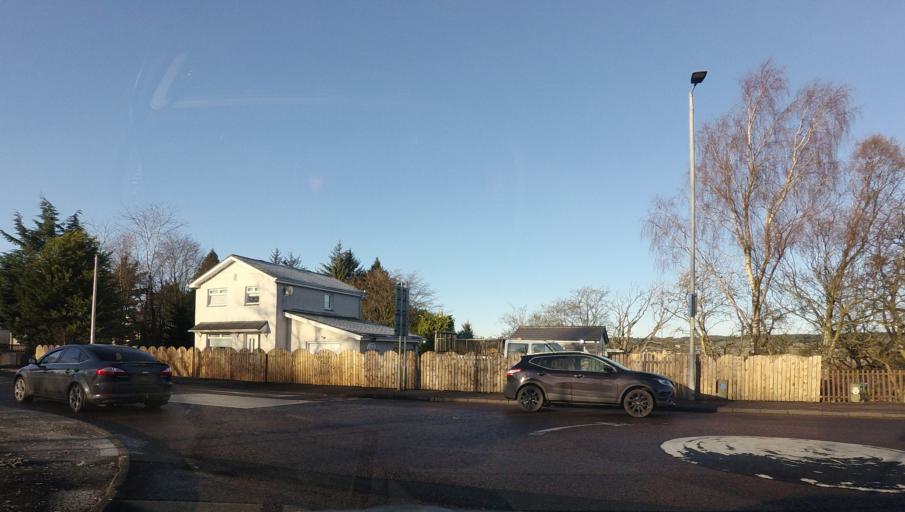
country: GB
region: Scotland
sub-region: North Lanarkshire
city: Shotts
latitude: 55.8021
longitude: -3.8252
